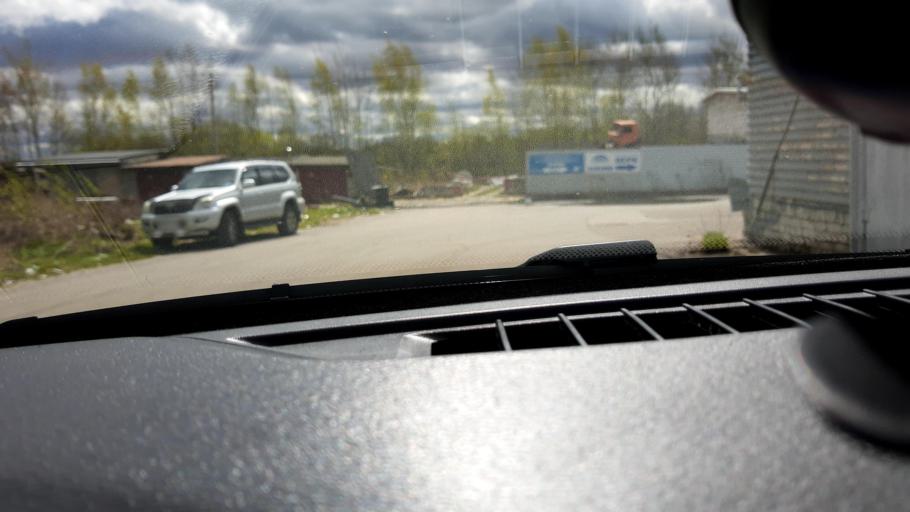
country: RU
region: Nizjnij Novgorod
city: Gorbatovka
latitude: 56.3094
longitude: 43.7984
